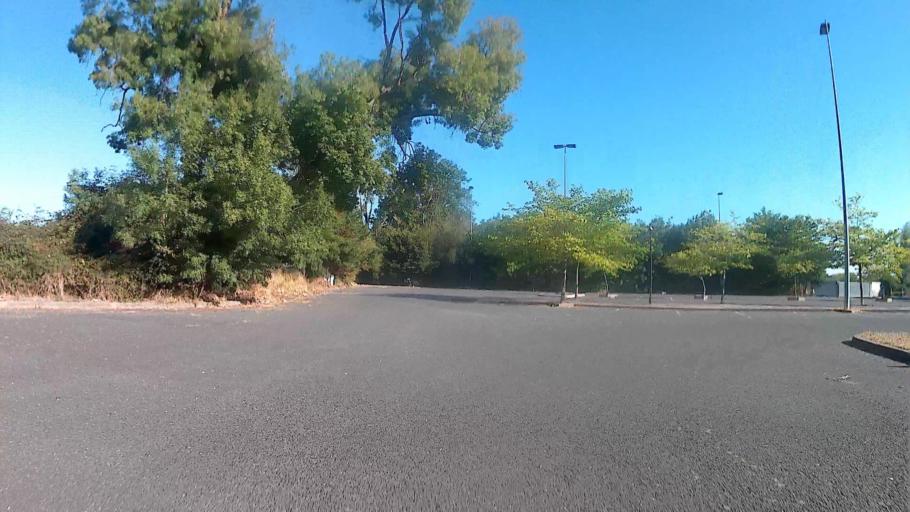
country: FR
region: Aquitaine
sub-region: Departement de la Gironde
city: Villenave-d'Ornon
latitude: 44.7897
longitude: -0.5257
